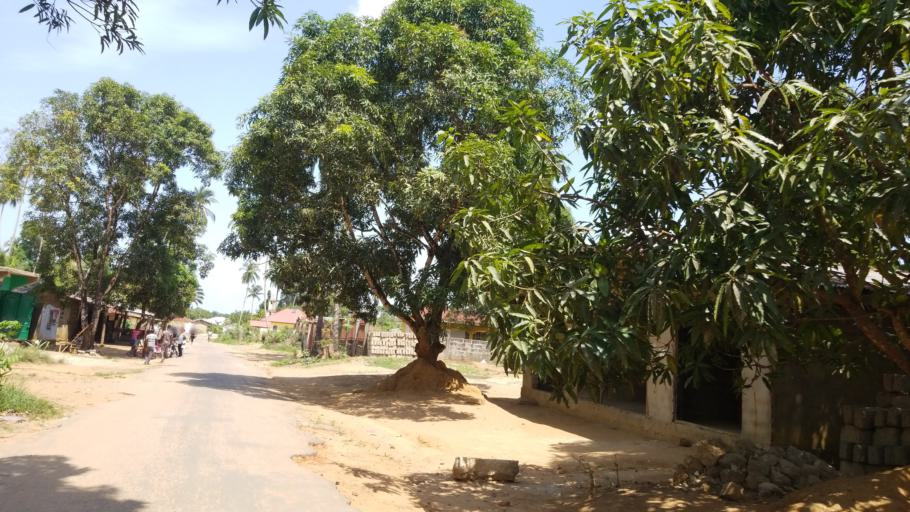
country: SL
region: Western Area
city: Waterloo
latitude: 8.3081
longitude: -13.0516
